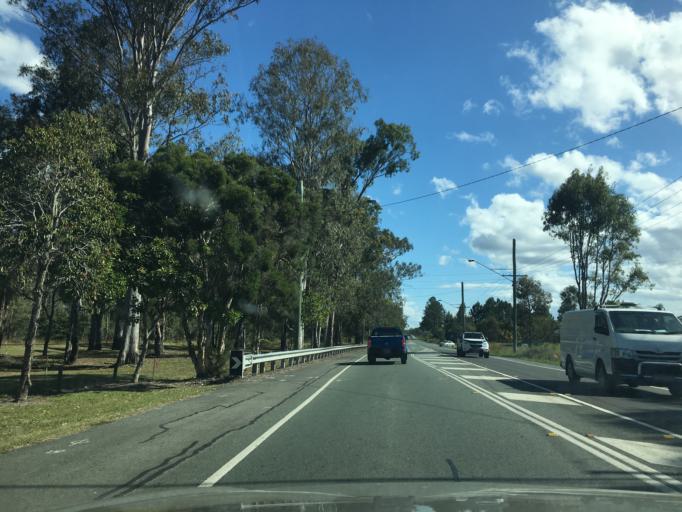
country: AU
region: Queensland
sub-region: Logan
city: Chambers Flat
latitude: -27.7699
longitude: 153.1067
